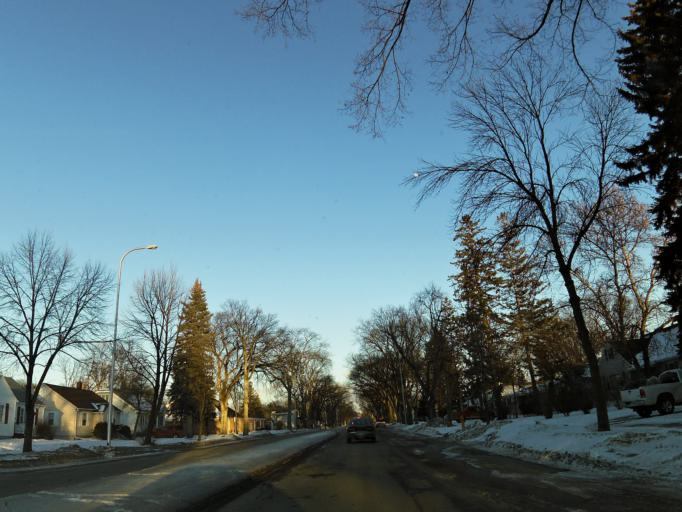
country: US
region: North Dakota
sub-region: Grand Forks County
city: Grand Forks
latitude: 47.9222
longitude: -97.0594
